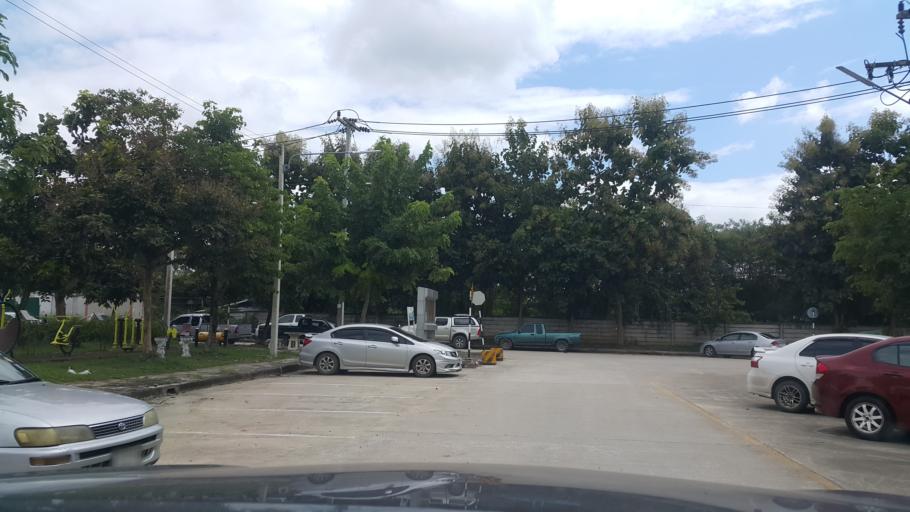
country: TH
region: Chiang Mai
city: Hang Dong
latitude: 18.7345
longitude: 98.9408
